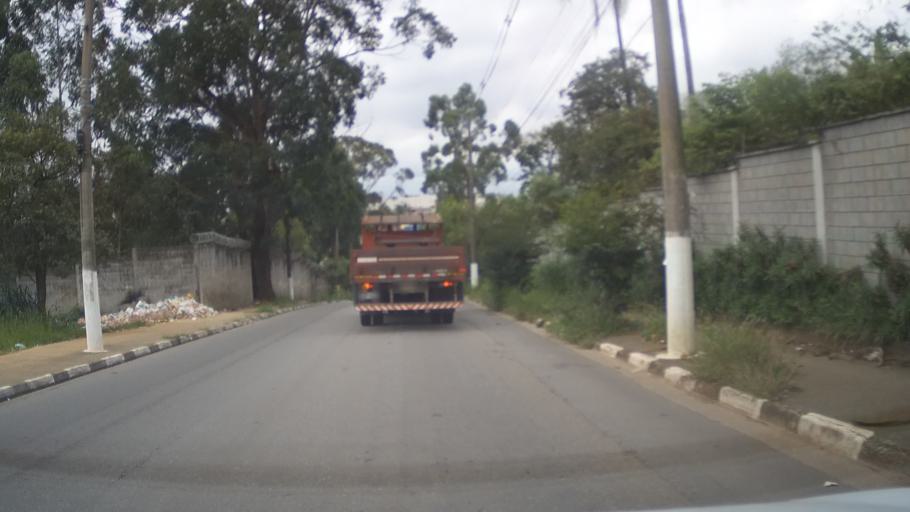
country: BR
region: Sao Paulo
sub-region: Itaquaquecetuba
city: Itaquaquecetuba
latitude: -23.4441
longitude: -46.3960
